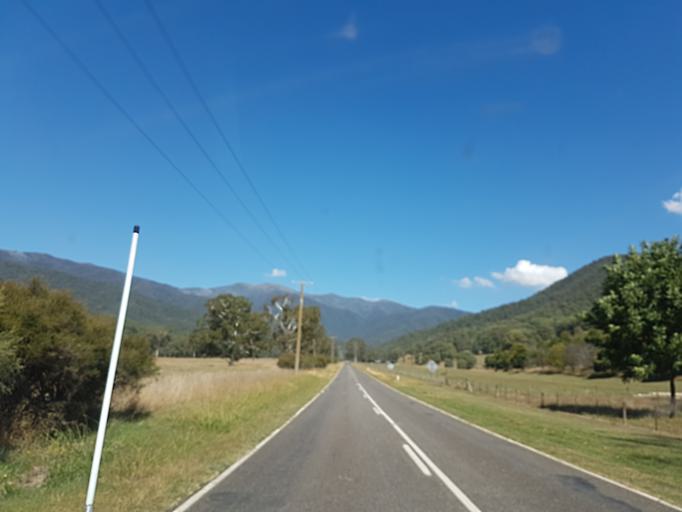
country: AU
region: Victoria
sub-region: Alpine
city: Mount Beauty
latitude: -36.8210
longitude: 147.0659
